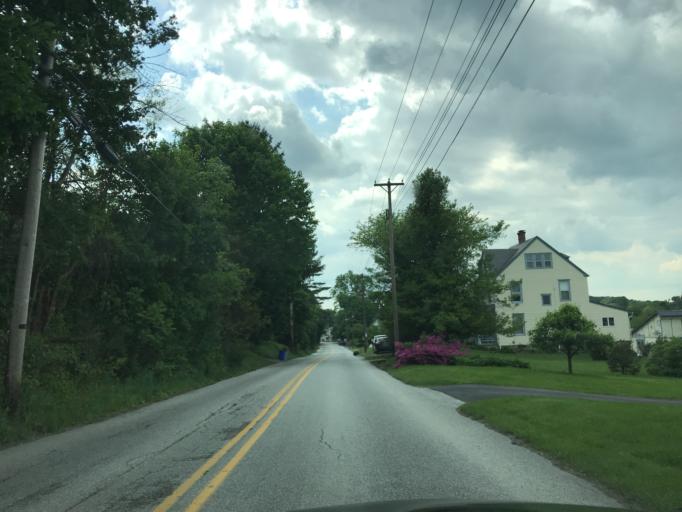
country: US
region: Pennsylvania
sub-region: York County
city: Susquehanna Trails
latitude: 39.7313
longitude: -76.3161
